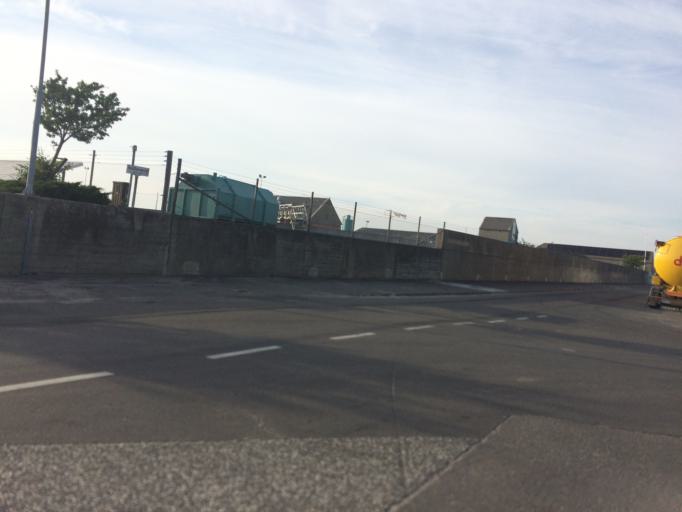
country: DK
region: Capital Region
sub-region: Bornholm Kommune
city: Ronne
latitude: 55.1009
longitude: 14.6876
